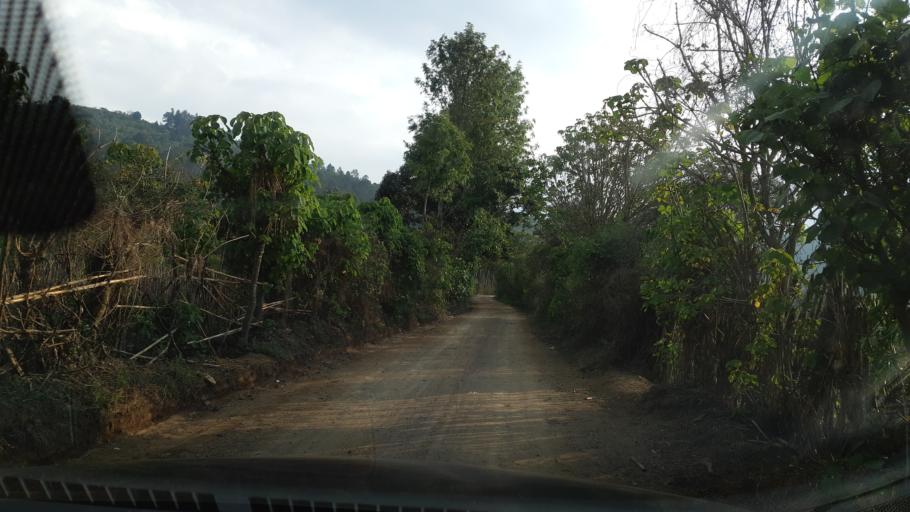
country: GT
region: Chimaltenango
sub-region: Municipio de Chimaltenango
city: Chimaltenango
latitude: 14.6541
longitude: -90.8432
